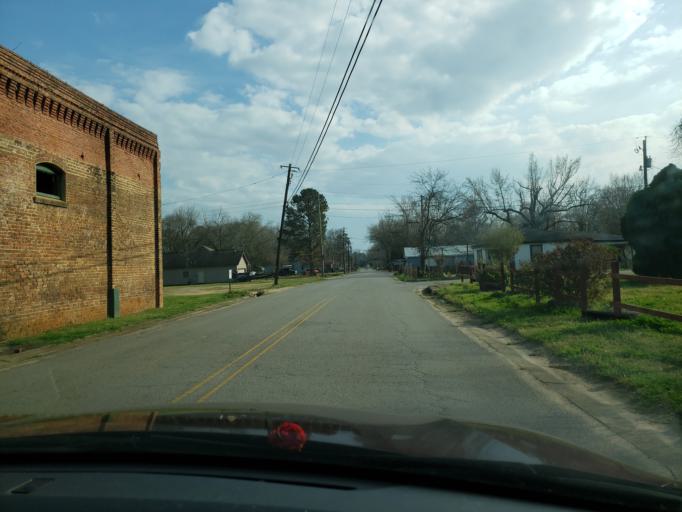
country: US
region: Alabama
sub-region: Hale County
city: Greensboro
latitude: 32.6990
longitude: -87.6093
